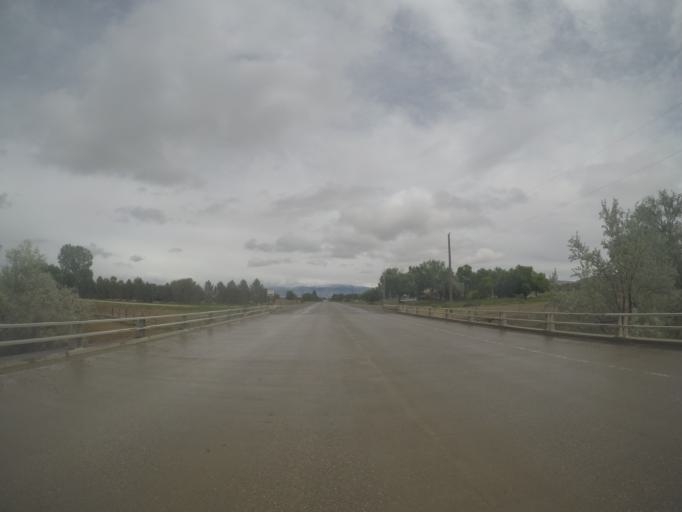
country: US
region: Wyoming
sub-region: Big Horn County
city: Lovell
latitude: 44.8406
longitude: -108.3530
